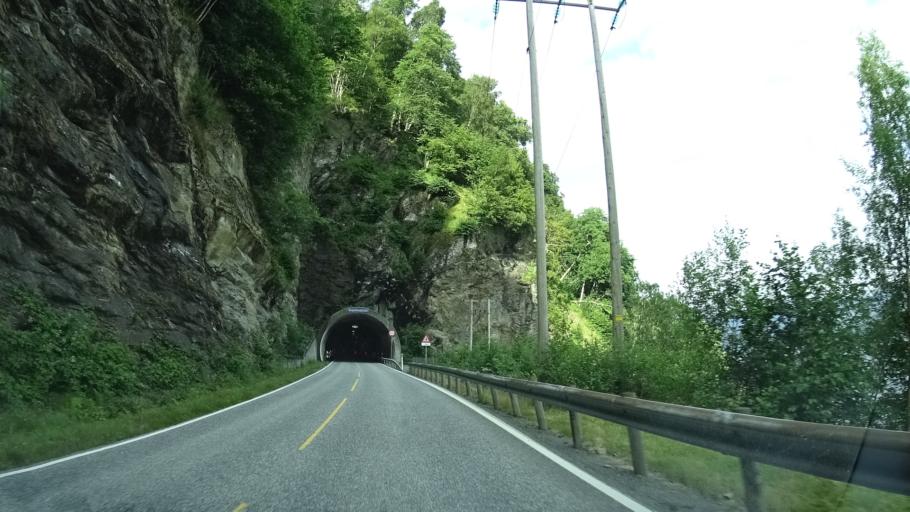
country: NO
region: Hordaland
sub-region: Kvam
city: Norheimsund
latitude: 60.3225
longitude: 6.1809
